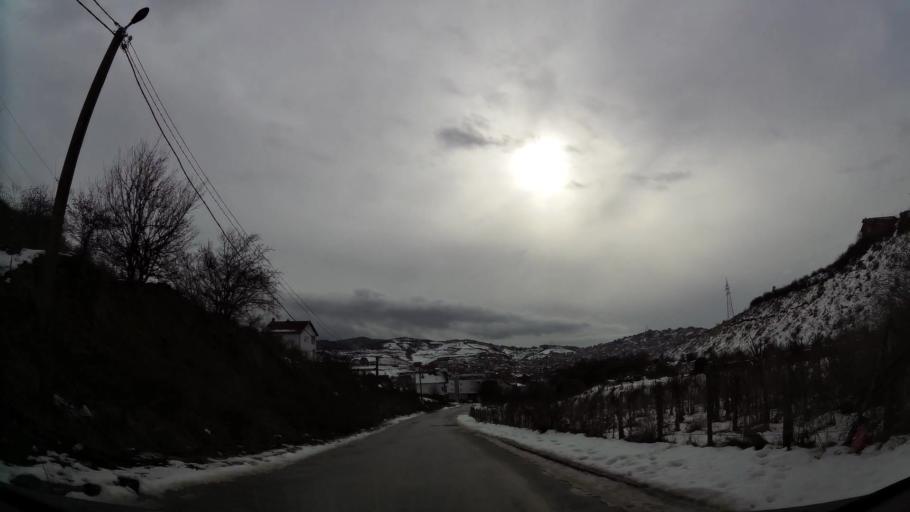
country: XK
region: Pristina
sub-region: Komuna e Prishtines
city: Pristina
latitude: 42.6908
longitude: 21.1769
